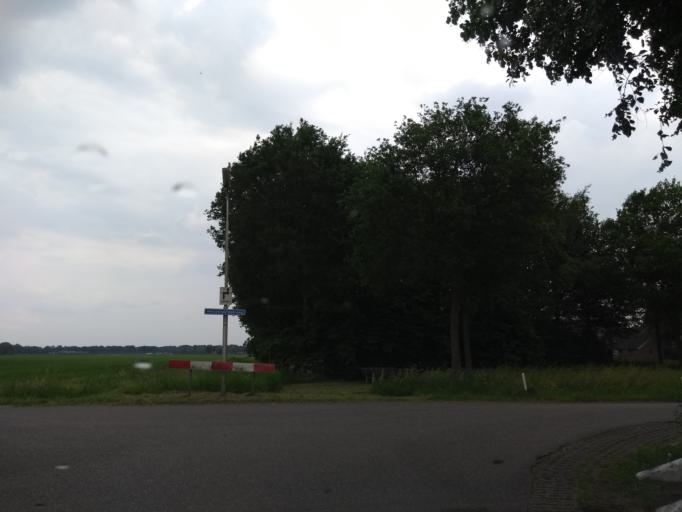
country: NL
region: Overijssel
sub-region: Gemeente Dalfsen
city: Dalfsen
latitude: 52.6183
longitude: 6.3515
